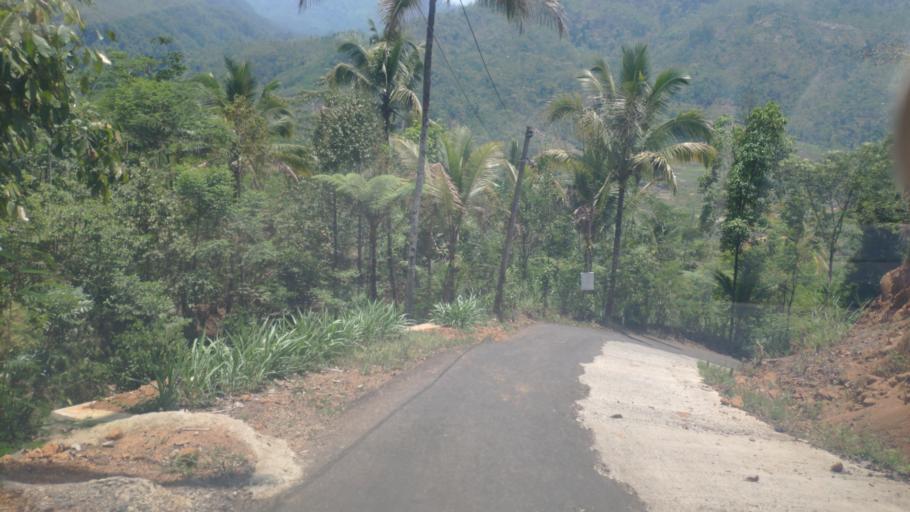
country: ID
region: Central Java
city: Purbalingga
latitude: -7.2910
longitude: 109.5872
